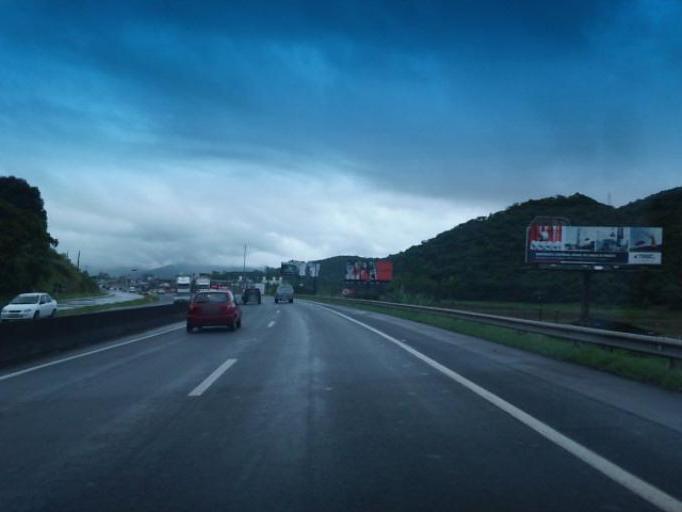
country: BR
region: Santa Catarina
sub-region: Itajai
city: Itajai
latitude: -26.9496
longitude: -48.6809
